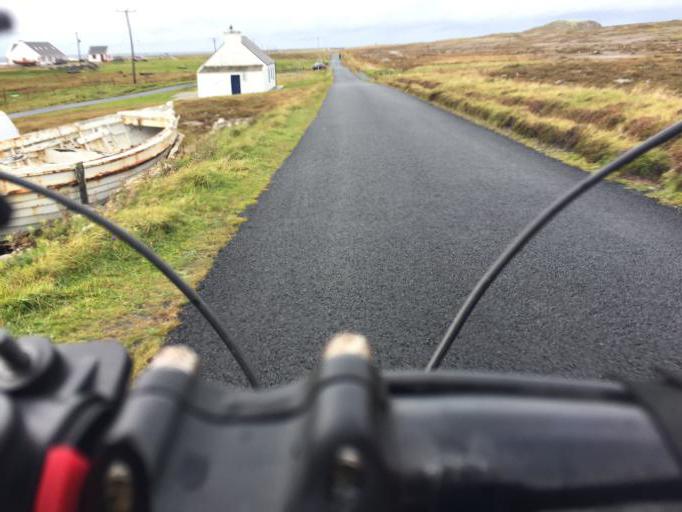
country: IE
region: Ulster
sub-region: County Donegal
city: Derrybeg
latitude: 55.2600
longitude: -8.2105
